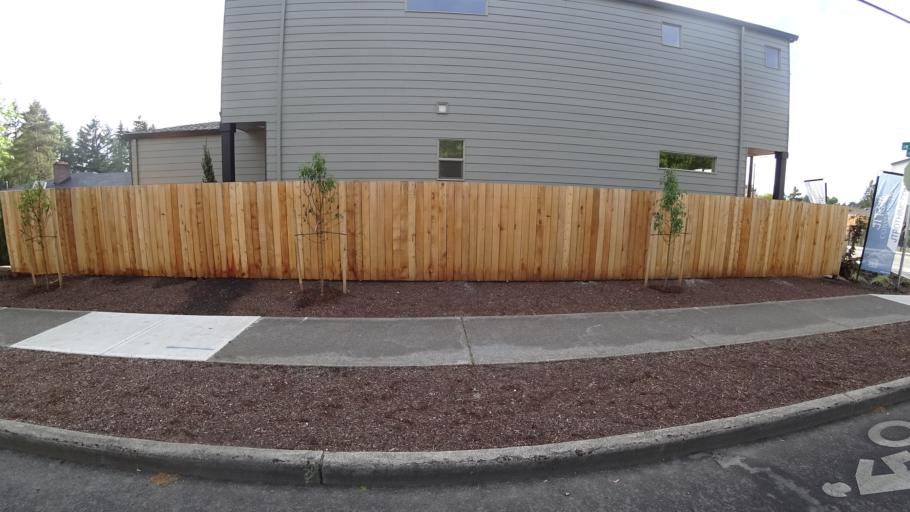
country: US
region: Oregon
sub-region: Washington County
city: Beaverton
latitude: 45.4838
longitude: -122.8260
